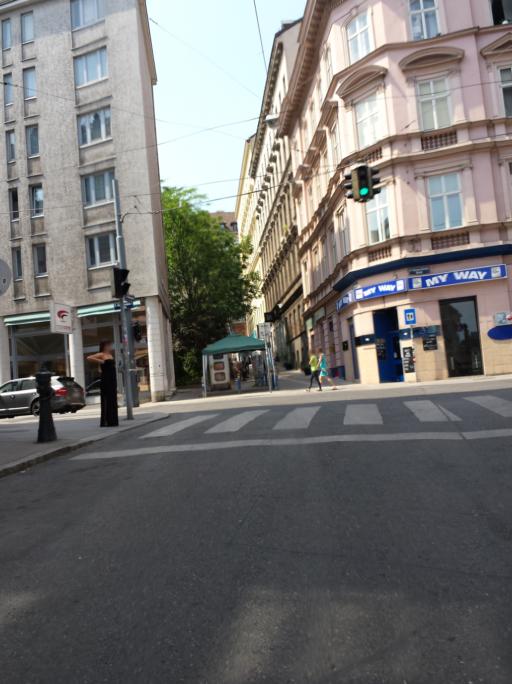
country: AT
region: Vienna
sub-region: Wien Stadt
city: Vienna
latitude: 48.1984
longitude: 16.3574
